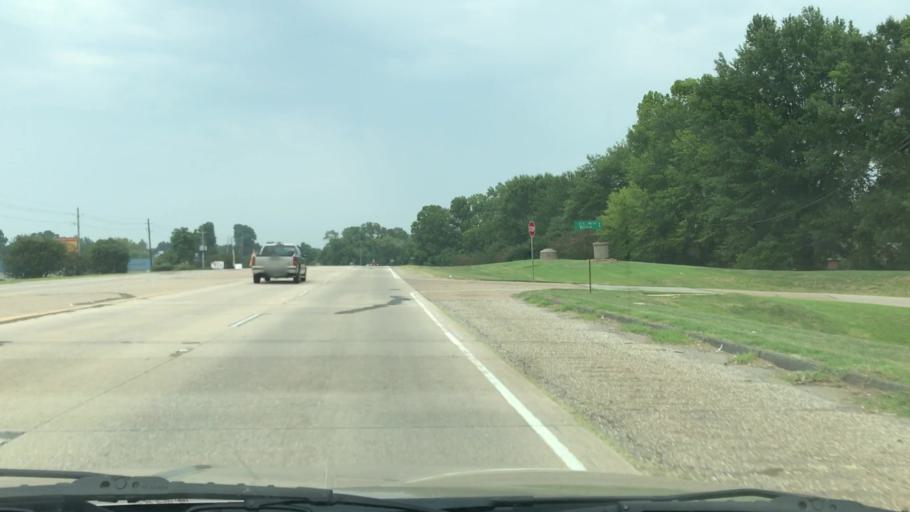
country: US
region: Louisiana
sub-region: Bossier Parish
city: Bossier City
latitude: 32.4415
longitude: -93.7047
